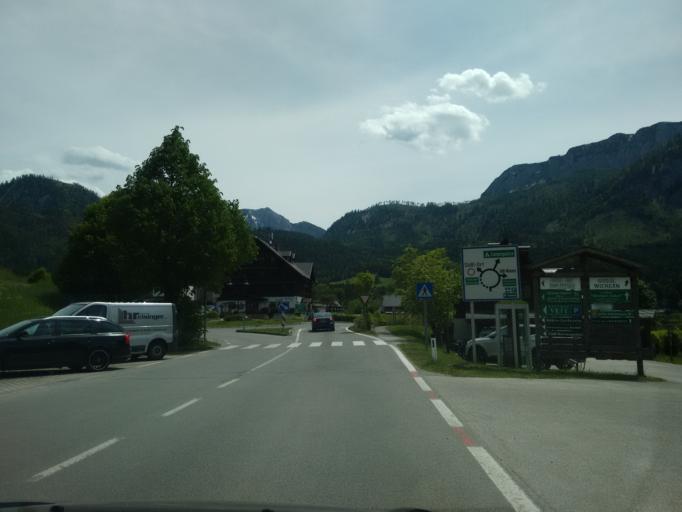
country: AT
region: Styria
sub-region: Politischer Bezirk Liezen
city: Bad Aussee
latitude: 47.6392
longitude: 13.9017
